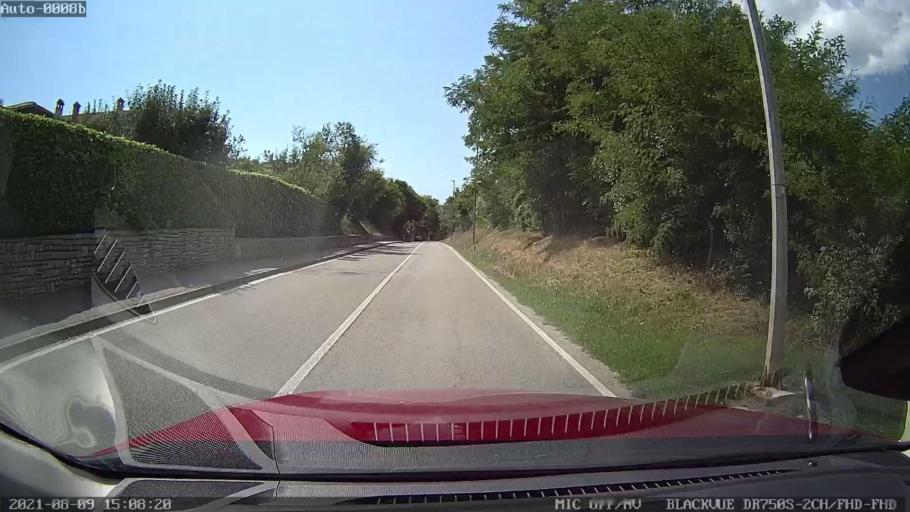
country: HR
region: Istarska
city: Pazin
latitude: 45.2448
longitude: 13.9550
